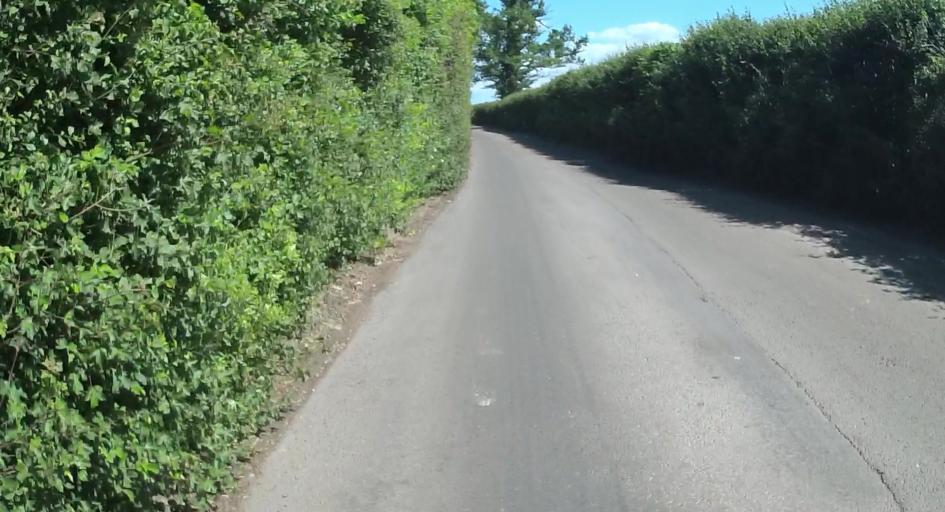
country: GB
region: England
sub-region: Hampshire
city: Hook
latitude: 51.3114
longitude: -0.9881
